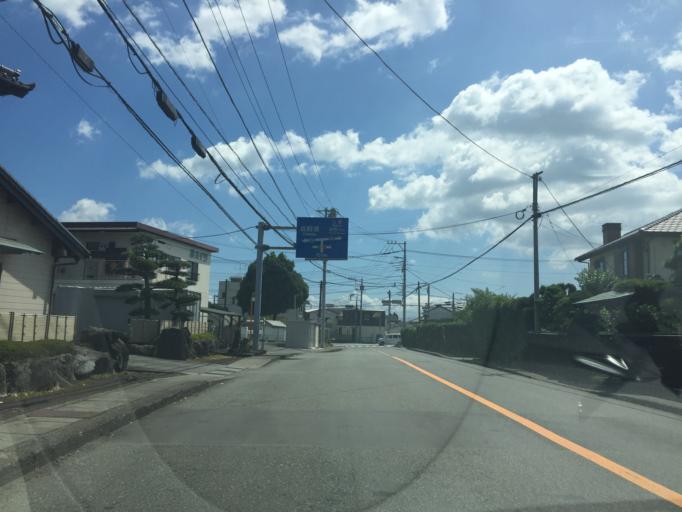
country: JP
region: Shizuoka
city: Mishima
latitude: 35.1822
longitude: 138.9061
